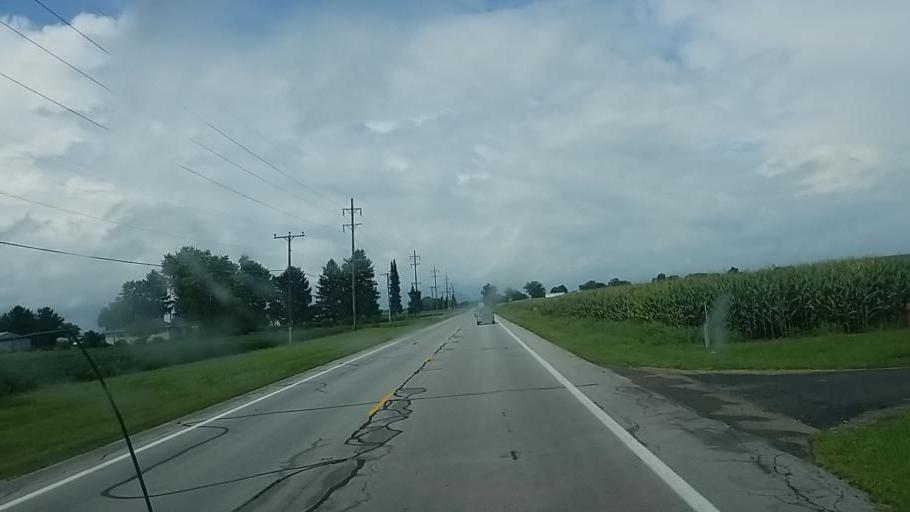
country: US
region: Ohio
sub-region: Logan County
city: West Liberty
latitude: 40.1860
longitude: -83.7423
